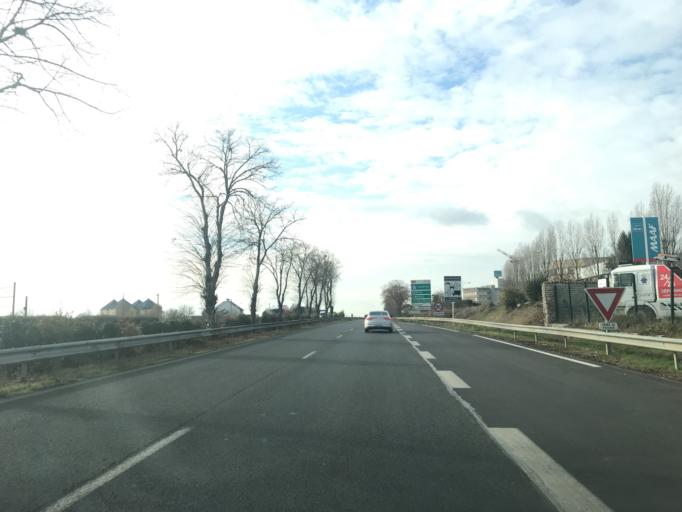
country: FR
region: Poitou-Charentes
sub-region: Departement des Deux-Sevres
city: Chauray
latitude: 46.3406
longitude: -0.3972
